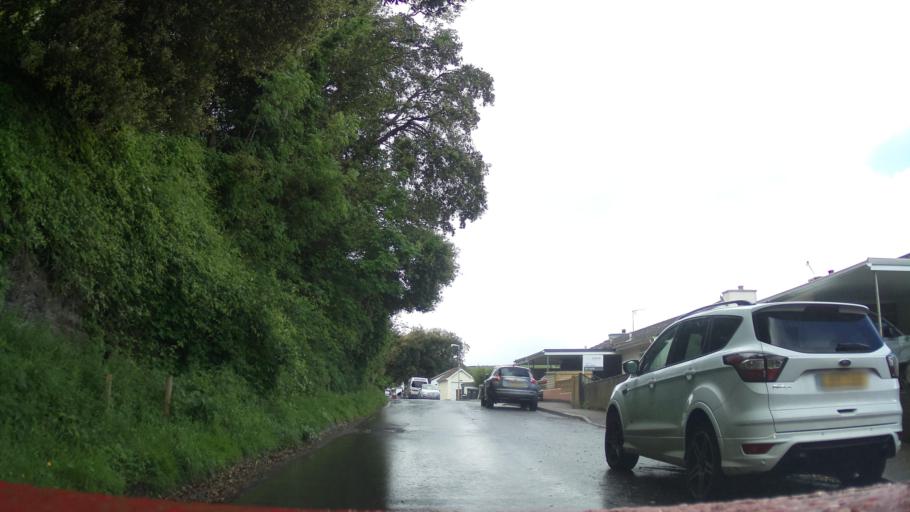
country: GB
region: England
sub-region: Devon
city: Dartmouth
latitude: 50.3518
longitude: -3.5632
